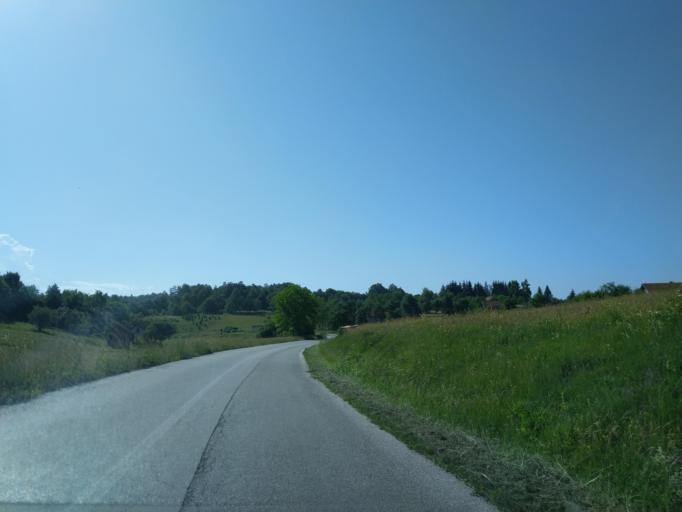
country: RS
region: Central Serbia
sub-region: Zlatiborski Okrug
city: Uzice
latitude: 43.8792
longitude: 19.7489
